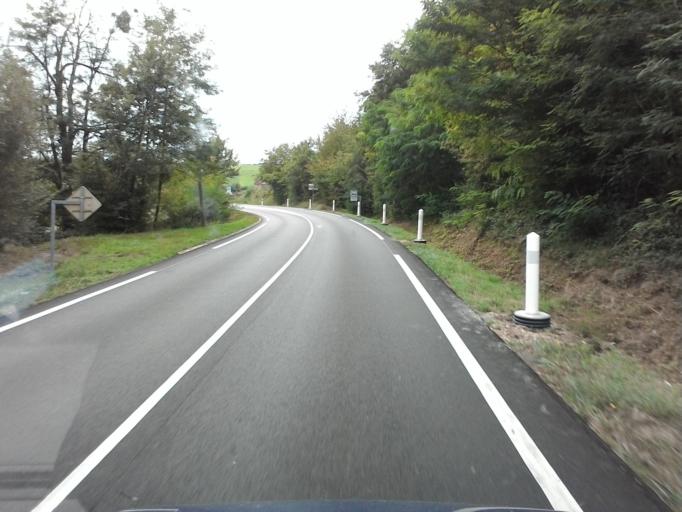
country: FR
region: Bourgogne
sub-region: Departement de Saone-et-Loire
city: Saint-Vallier
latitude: 46.6031
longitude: 4.4745
